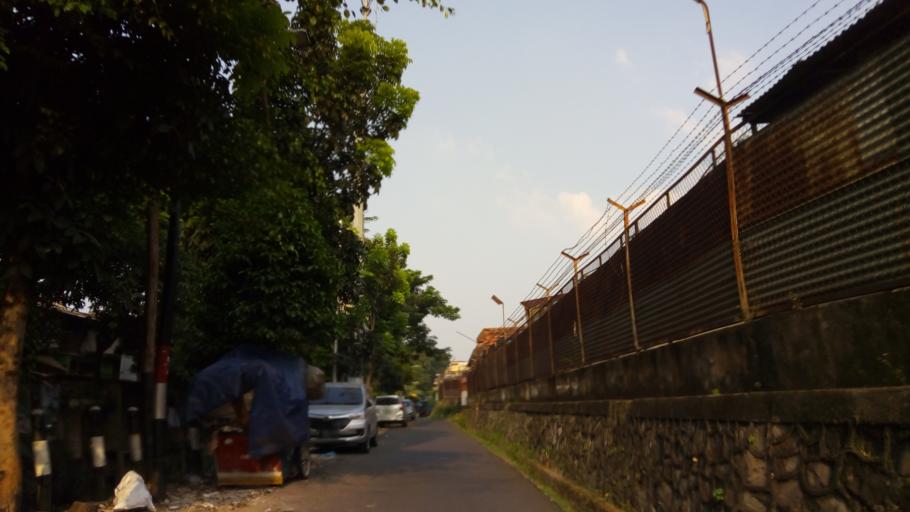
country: ID
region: Jakarta Raya
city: Jakarta
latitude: -6.1947
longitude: 106.8522
